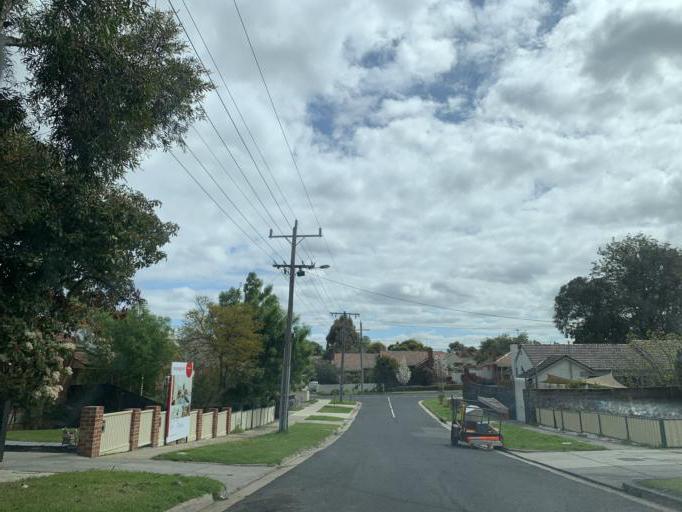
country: AU
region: Victoria
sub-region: Darebin
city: Reservoir
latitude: -37.7327
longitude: 144.9844
